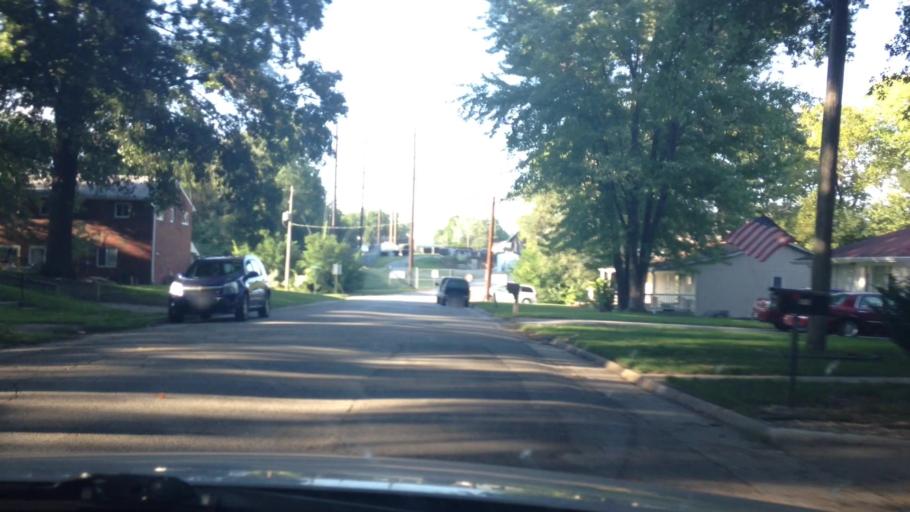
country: US
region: Kansas
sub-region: Leavenworth County
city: Leavenworth
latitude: 39.2968
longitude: -94.9264
